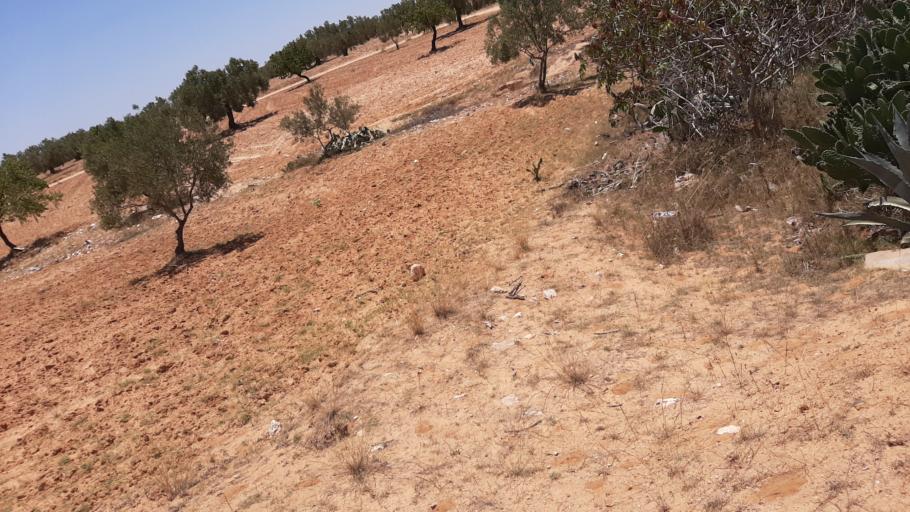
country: TN
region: Al Mahdiyah
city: El Jem
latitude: 35.0973
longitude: 10.6496
